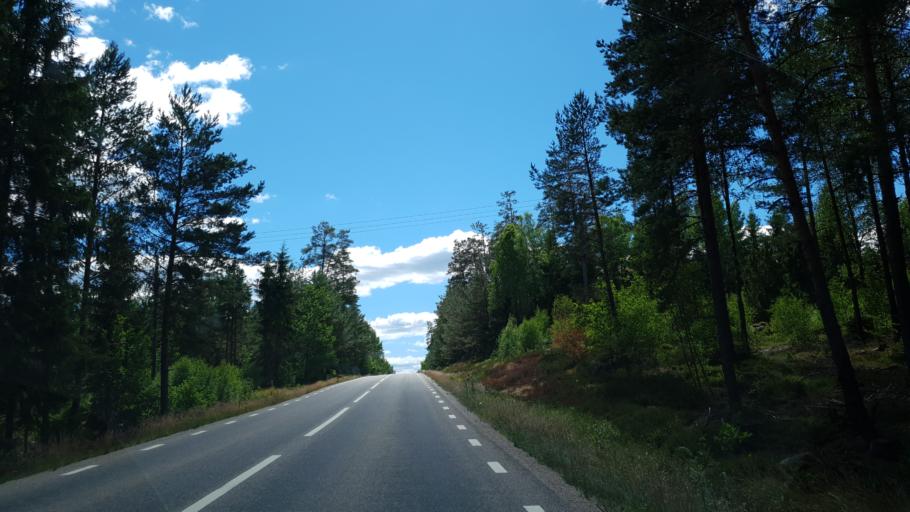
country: SE
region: Kronoberg
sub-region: Lessebo Kommun
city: Lessebo
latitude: 56.7620
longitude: 15.2895
